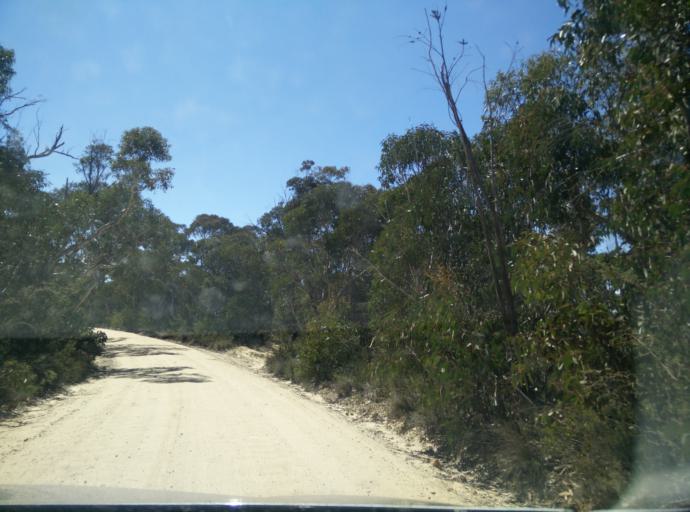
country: AU
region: New South Wales
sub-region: Blue Mountains Municipality
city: Blackheath
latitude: -33.5790
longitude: 150.2767
